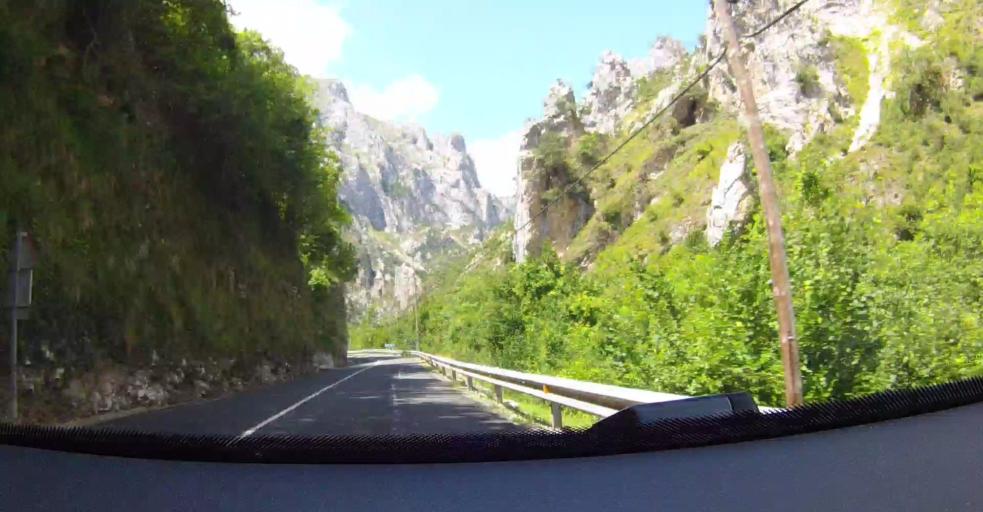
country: ES
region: Cantabria
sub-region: Provincia de Cantabria
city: Tresviso
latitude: 43.2648
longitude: -4.6250
